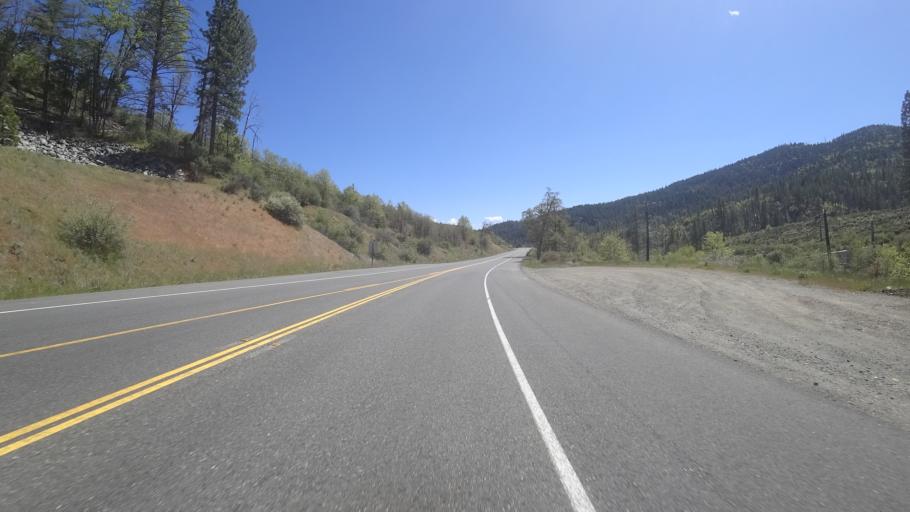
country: US
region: California
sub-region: Trinity County
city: Weaverville
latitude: 40.7421
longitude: -122.9679
